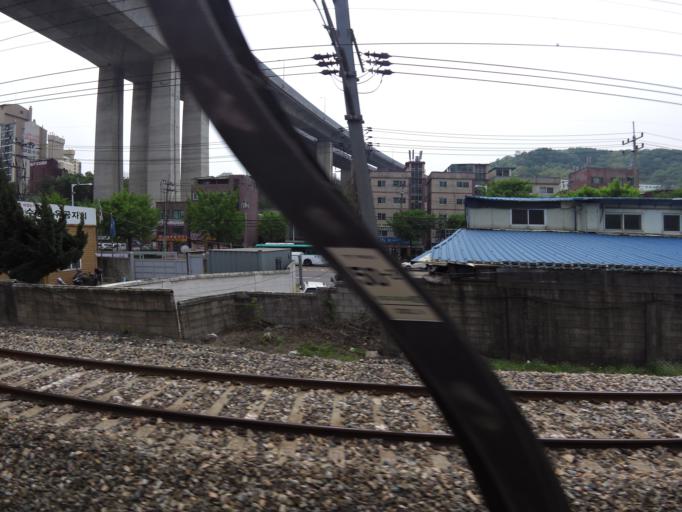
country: KR
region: Gyeonggi-do
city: Anyang-si
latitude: 37.3786
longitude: 126.9397
